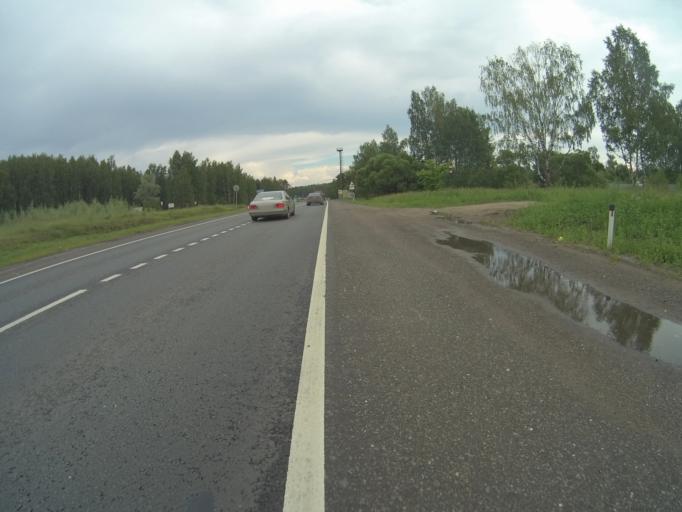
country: RU
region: Vladimir
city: Kameshkovo
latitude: 56.1946
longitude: 40.9194
